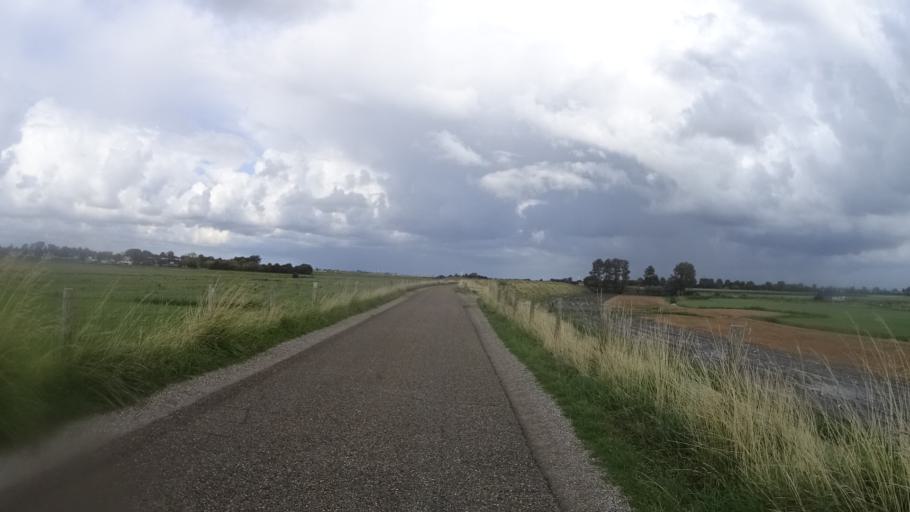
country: NL
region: North Holland
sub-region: Gemeente Schagen
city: Schagen
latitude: 52.7924
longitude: 4.7619
